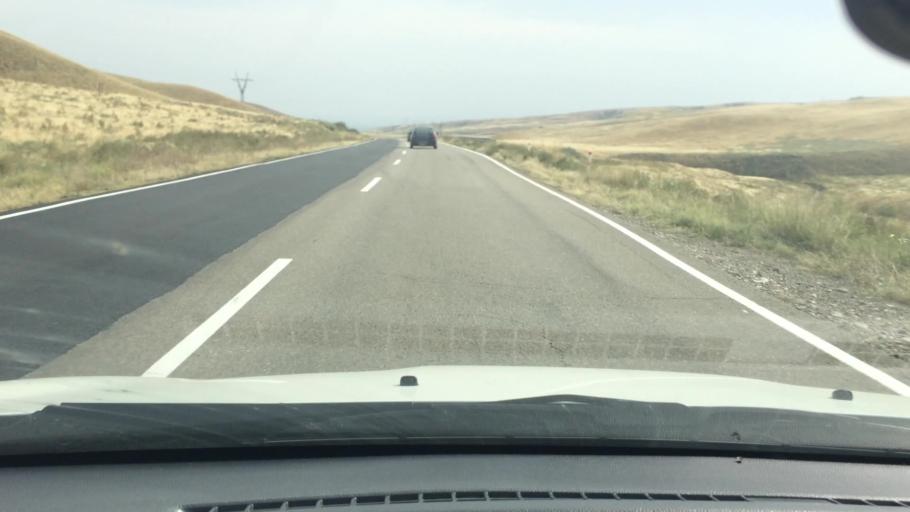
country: GE
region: Kvemo Kartli
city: Rust'avi
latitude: 41.5118
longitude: 44.9475
